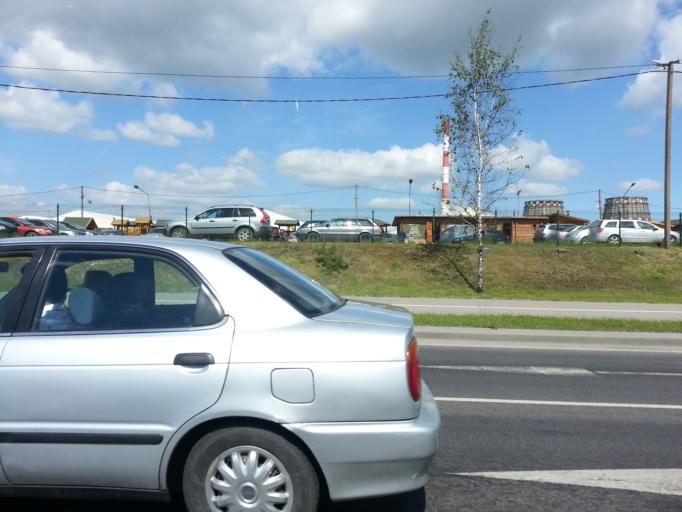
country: LT
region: Vilnius County
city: Pilaite
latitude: 54.6596
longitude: 25.1616
